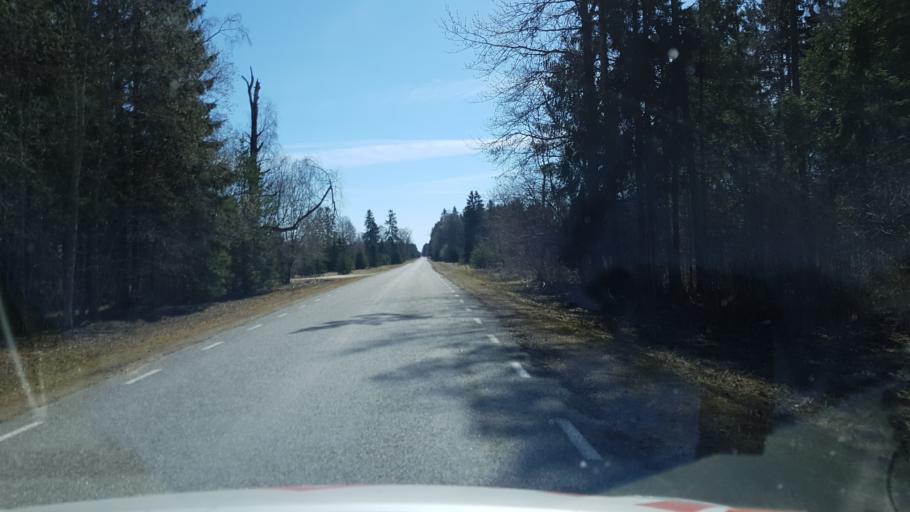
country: EE
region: Laeaene-Virumaa
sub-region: Vinni vald
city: Vinni
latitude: 59.1680
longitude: 26.5089
